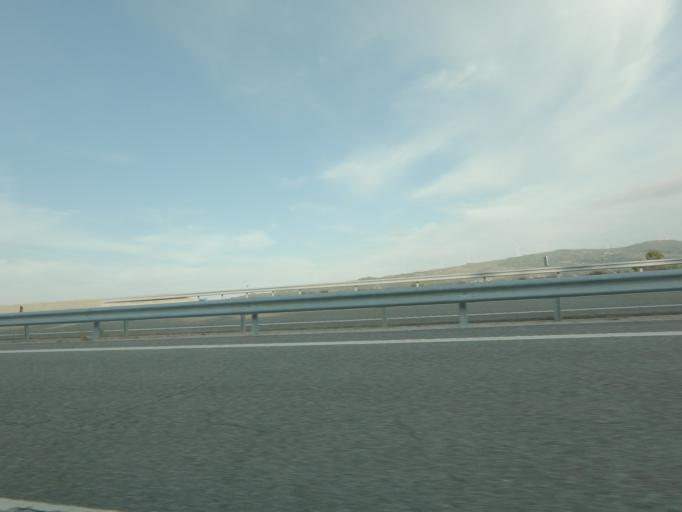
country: PT
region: Vila Real
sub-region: Vila Pouca de Aguiar
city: Vila Pouca de Aguiar
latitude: 41.4955
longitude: -7.6571
